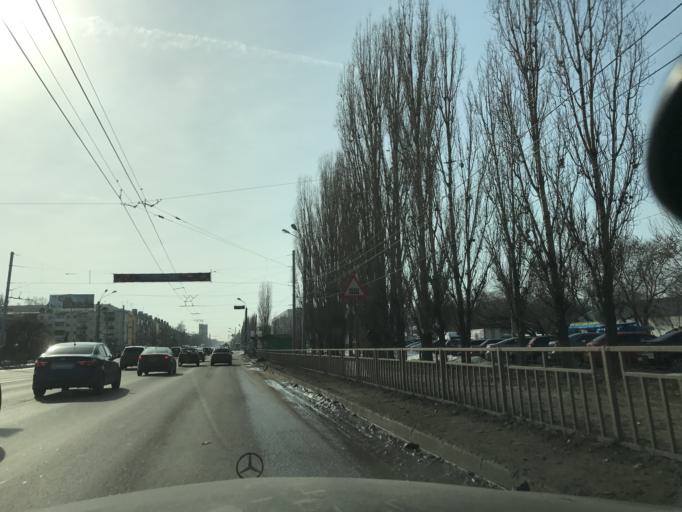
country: RU
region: Nizjnij Novgorod
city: Nizhniy Novgorod
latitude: 56.2860
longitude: 43.9283
